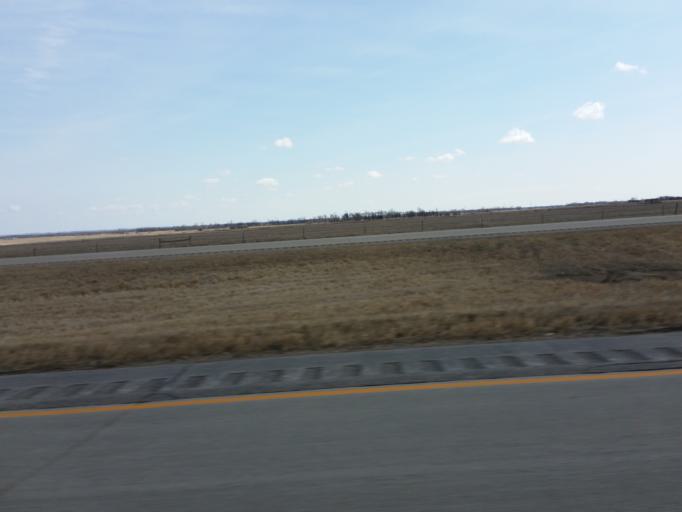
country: US
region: South Dakota
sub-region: Roberts County
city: Sisseton
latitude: 45.4376
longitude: -96.9935
